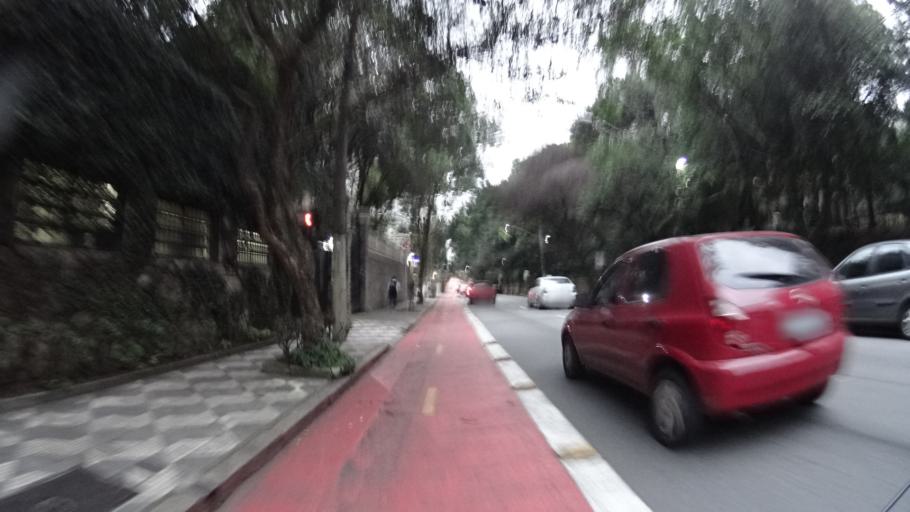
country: BR
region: Sao Paulo
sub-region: Sao Paulo
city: Sao Paulo
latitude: -23.5447
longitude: -46.6593
